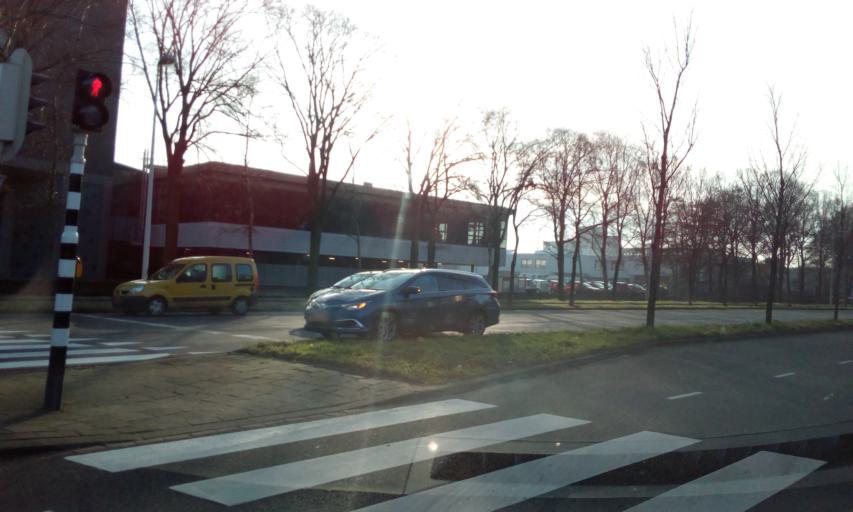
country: NL
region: South Holland
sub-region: Gemeente Westland
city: Kwintsheul
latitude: 52.0540
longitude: 4.2566
